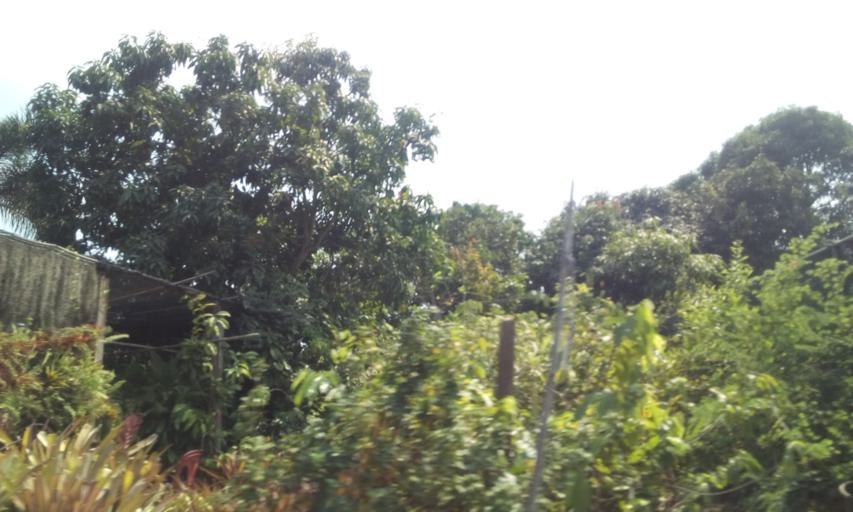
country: TH
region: Nakhon Nayok
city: Ongkharak
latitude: 14.1292
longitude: 100.9490
